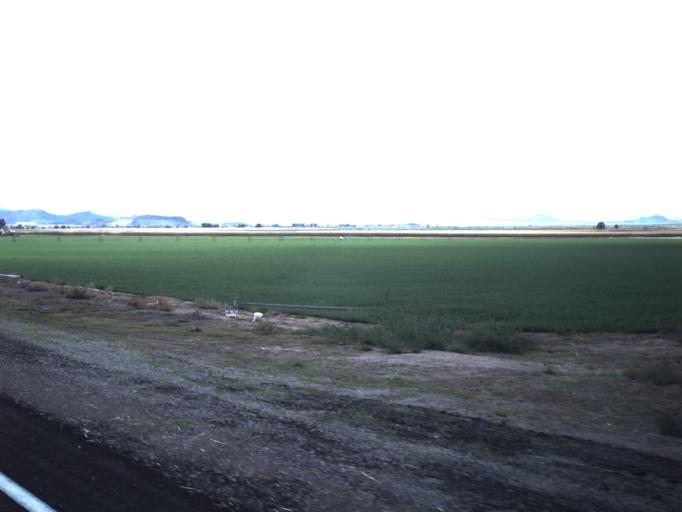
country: US
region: Utah
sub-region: Millard County
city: Fillmore
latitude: 38.8668
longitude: -112.4166
